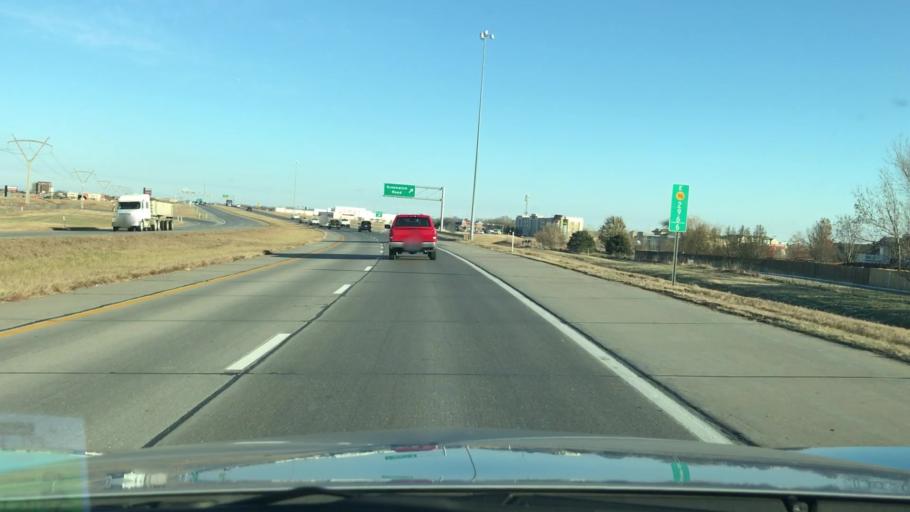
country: US
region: Kansas
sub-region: Sedgwick County
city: Bellaire
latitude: 37.7301
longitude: -97.2152
